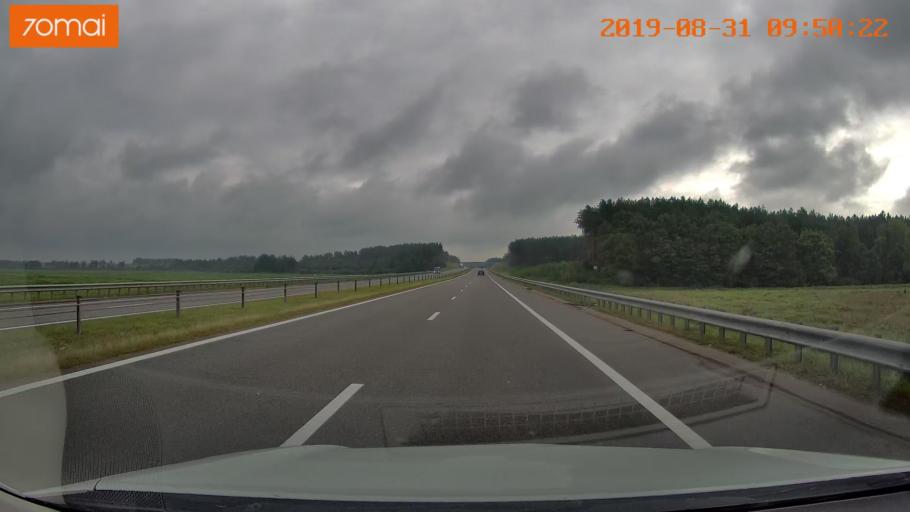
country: BY
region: Mogilev
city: Byalynichy
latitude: 53.9653
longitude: 29.7157
